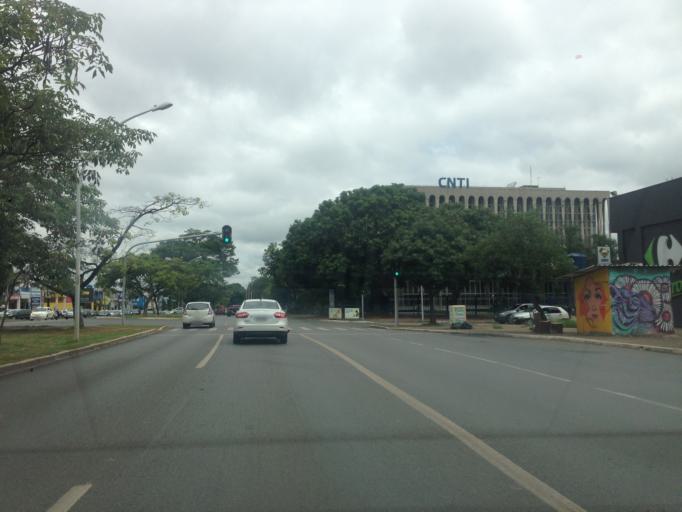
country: BR
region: Federal District
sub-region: Brasilia
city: Brasilia
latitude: -15.7750
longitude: -47.8881
